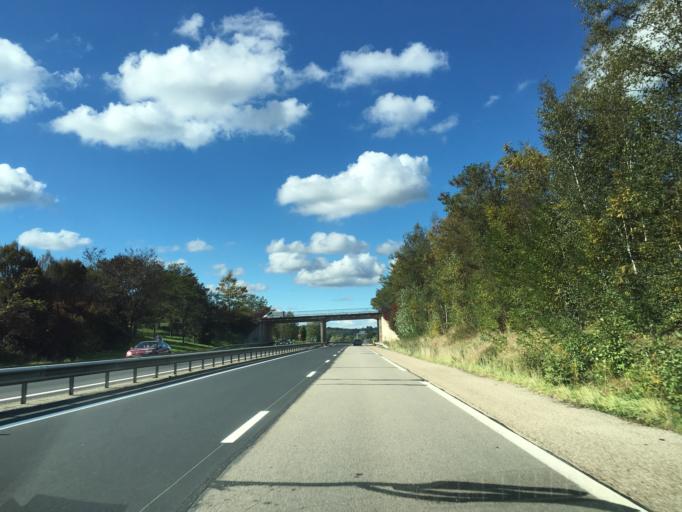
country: FR
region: Lorraine
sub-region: Departement des Vosges
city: Saint-Michel-sur-Meurthe
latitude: 48.3285
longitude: 6.9026
